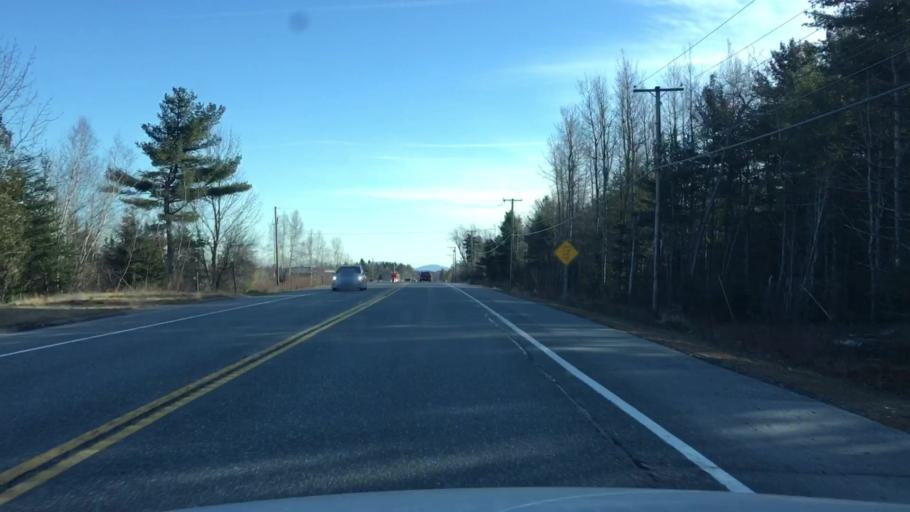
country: US
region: Maine
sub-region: Hancock County
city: Surry
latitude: 44.6194
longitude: -68.5290
